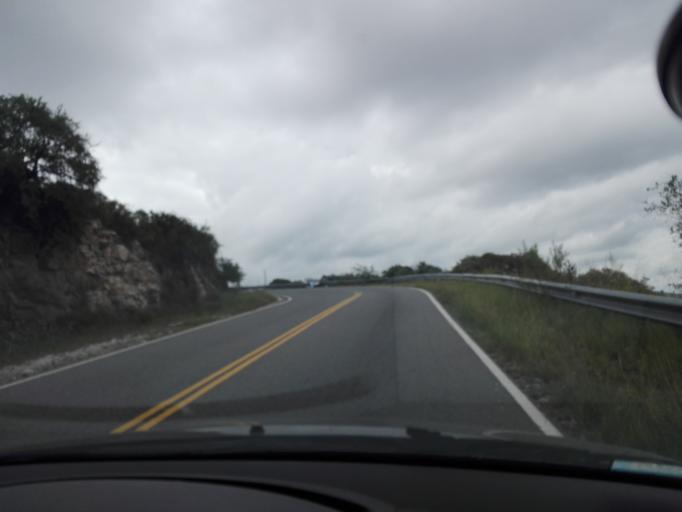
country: AR
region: Cordoba
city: Cuesta Blanca
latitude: -31.5940
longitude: -64.5297
